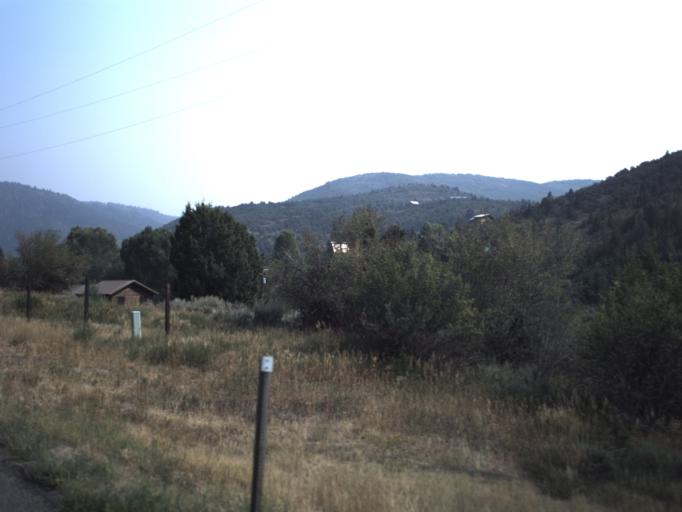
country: US
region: Utah
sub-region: Summit County
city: Francis
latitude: 40.6254
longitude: -111.2370
